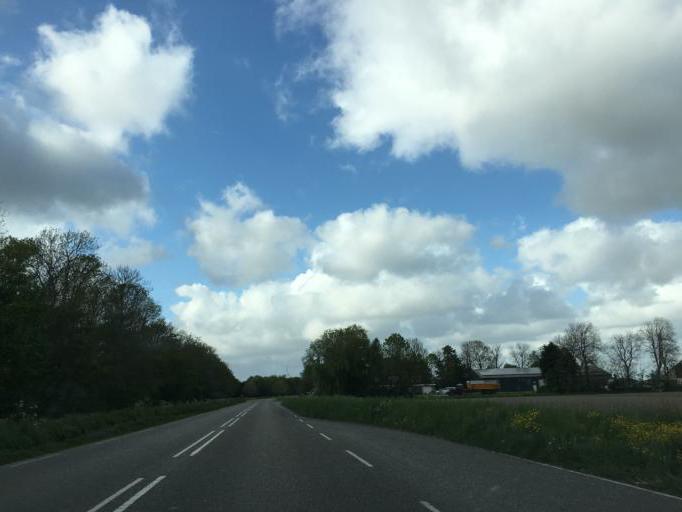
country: NL
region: North Holland
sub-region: Gemeente Opmeer
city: Opmeer
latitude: 52.7604
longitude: 4.9482
